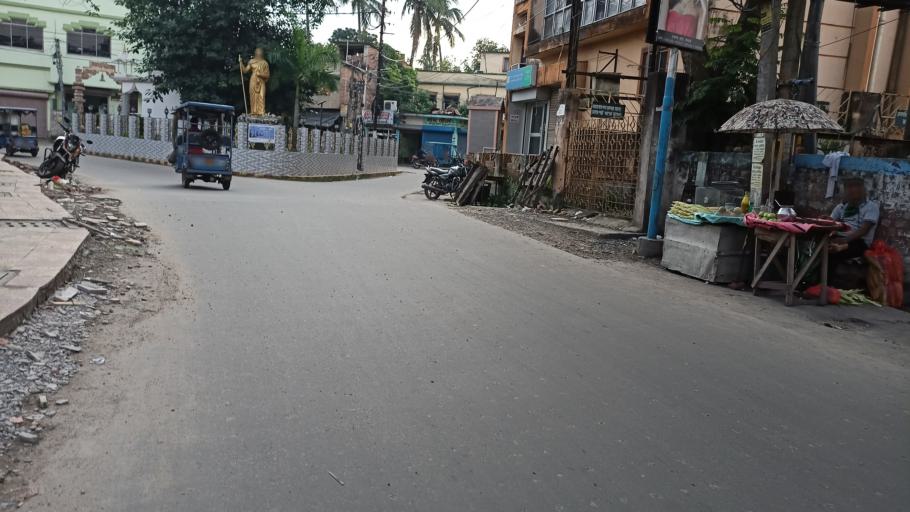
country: IN
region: West Bengal
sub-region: North 24 Parganas
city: Bangaon
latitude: 23.0455
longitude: 88.8288
